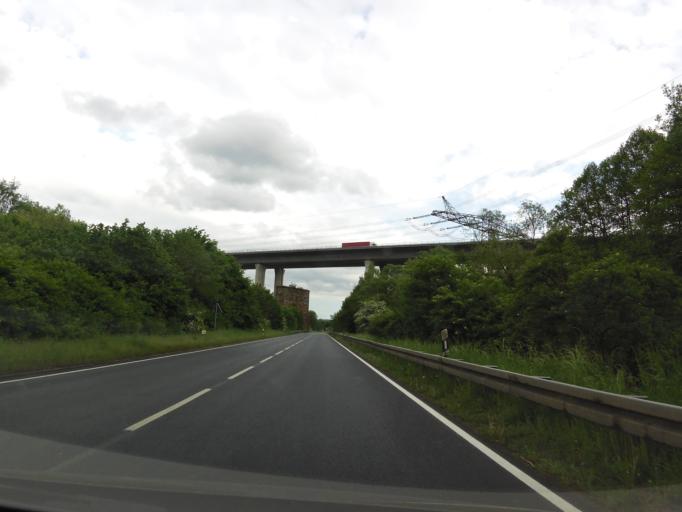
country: DE
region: Thuringia
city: Gerstungen
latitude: 50.9611
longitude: 10.0416
